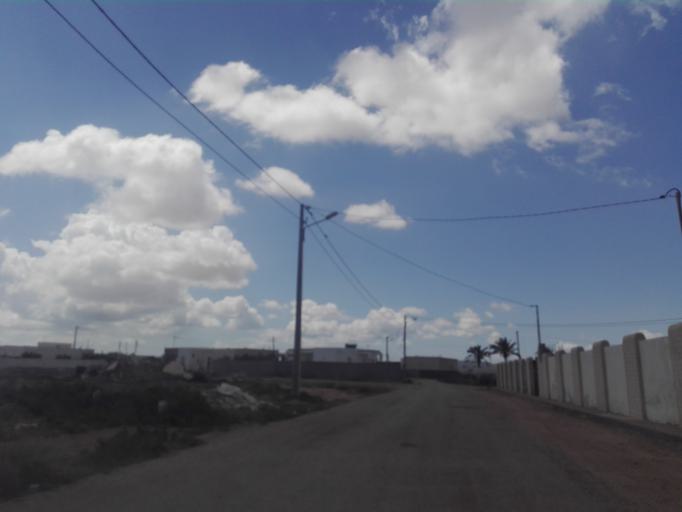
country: TN
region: Safaqis
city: Jabinyanah
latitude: 34.8229
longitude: 11.2534
